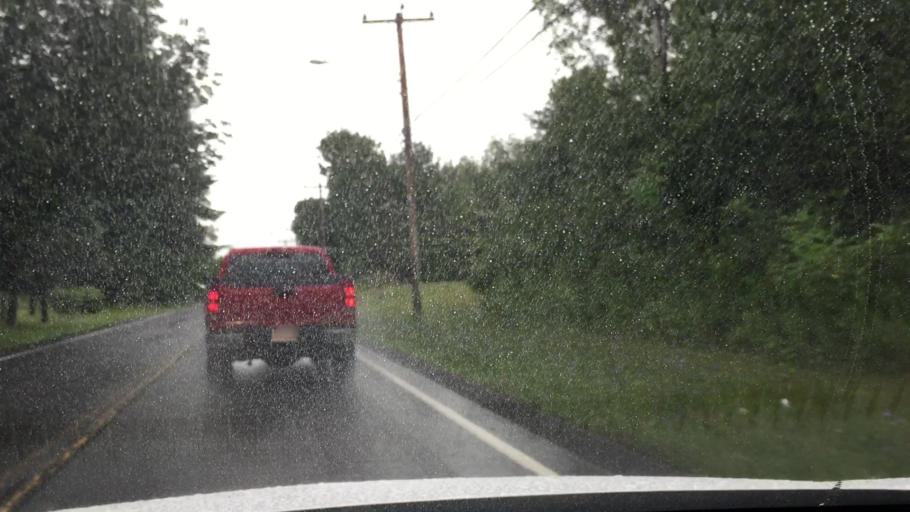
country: US
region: Massachusetts
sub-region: Berkshire County
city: Pittsfield
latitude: 42.4398
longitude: -73.2736
